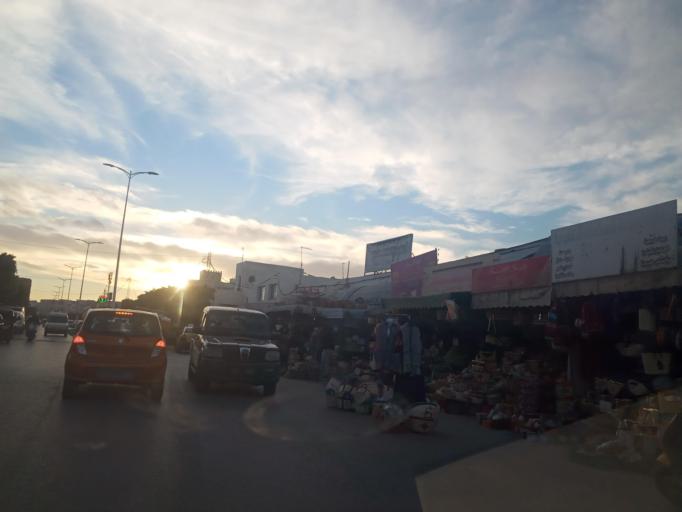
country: TN
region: Qabis
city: Gabes
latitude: 33.8887
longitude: 10.0953
